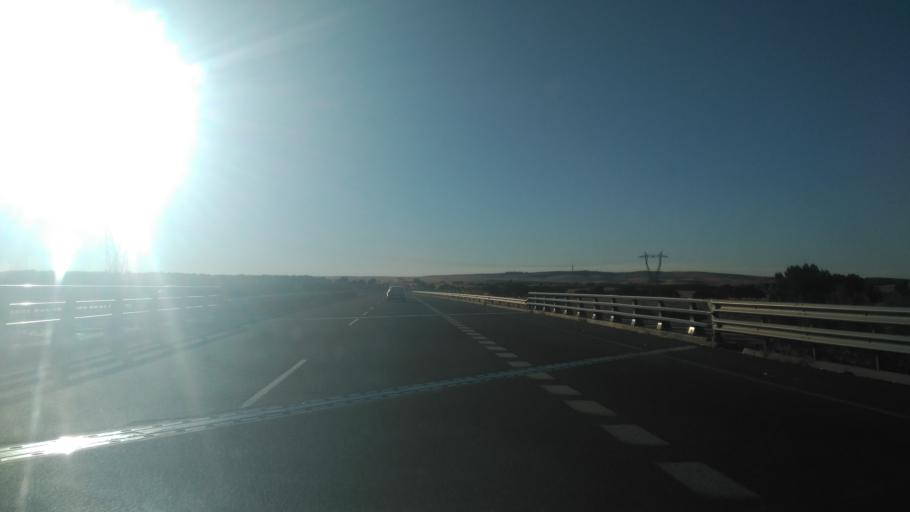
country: ES
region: Castille and Leon
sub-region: Provincia de Salamanca
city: Mozarbez
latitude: 40.8708
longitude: -5.6584
